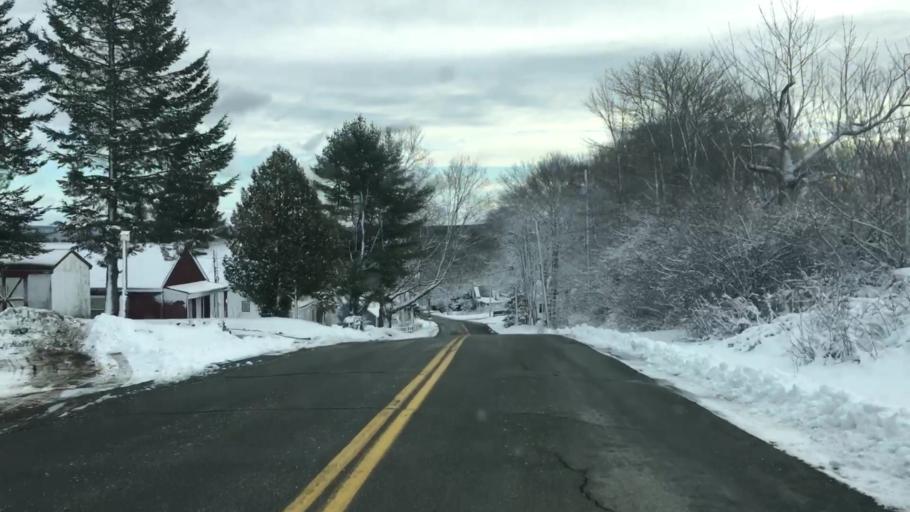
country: US
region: Maine
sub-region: Knox County
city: Rockland
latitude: 44.1107
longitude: -69.1266
